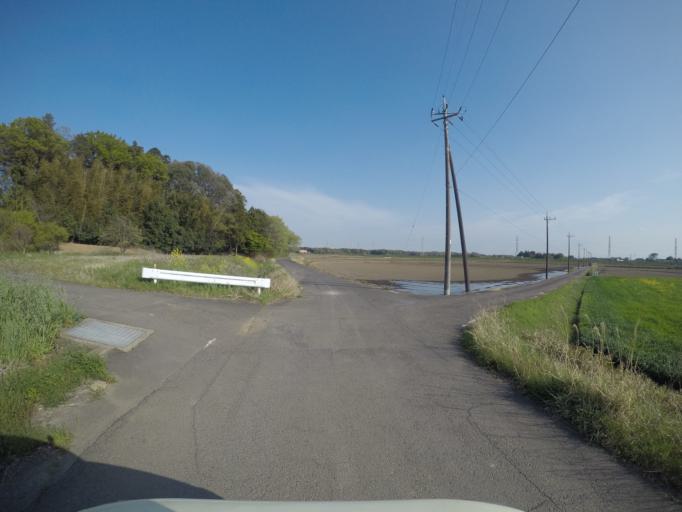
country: JP
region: Ibaraki
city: Ishige
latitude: 36.1858
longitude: 140.0085
